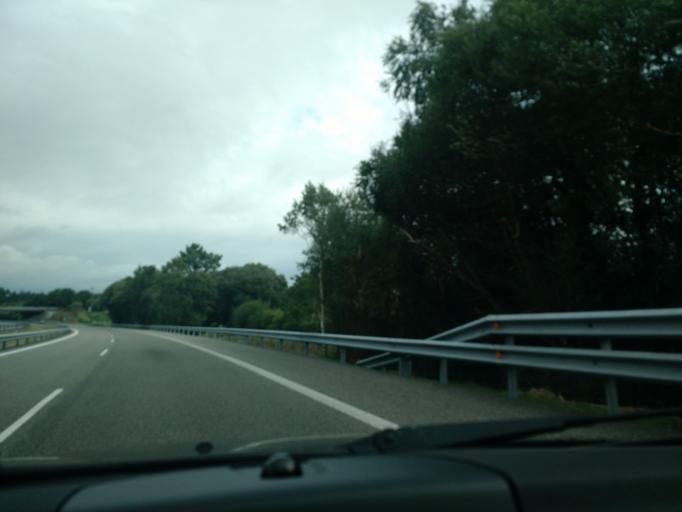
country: ES
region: Galicia
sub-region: Provincia da Coruna
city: Betanzos
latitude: 43.2680
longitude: -8.2528
